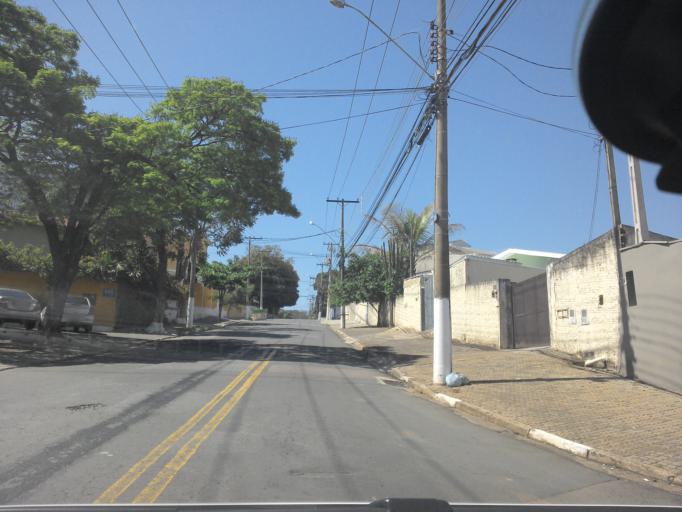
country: BR
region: Sao Paulo
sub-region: Campinas
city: Campinas
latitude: -22.8477
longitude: -47.0441
